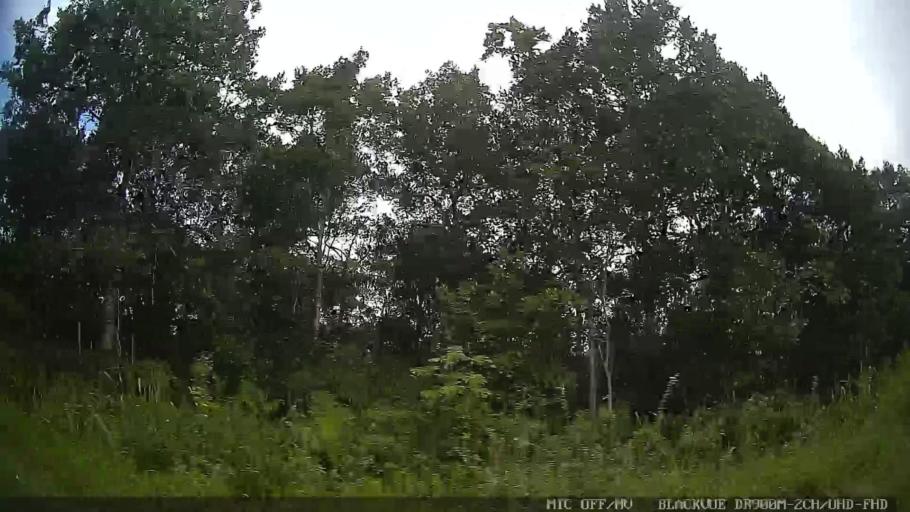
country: BR
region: Sao Paulo
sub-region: Iguape
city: Iguape
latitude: -24.6629
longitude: -47.4275
